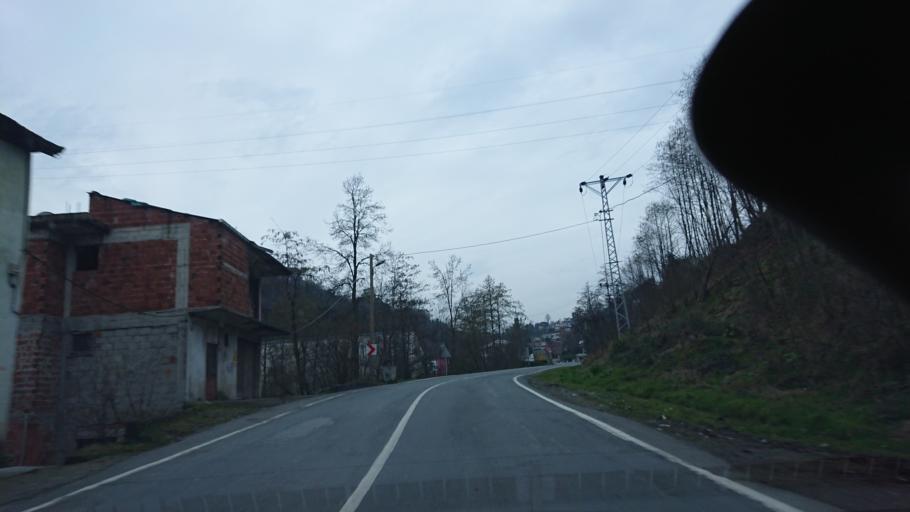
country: TR
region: Rize
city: Rize
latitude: 41.0280
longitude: 40.5067
